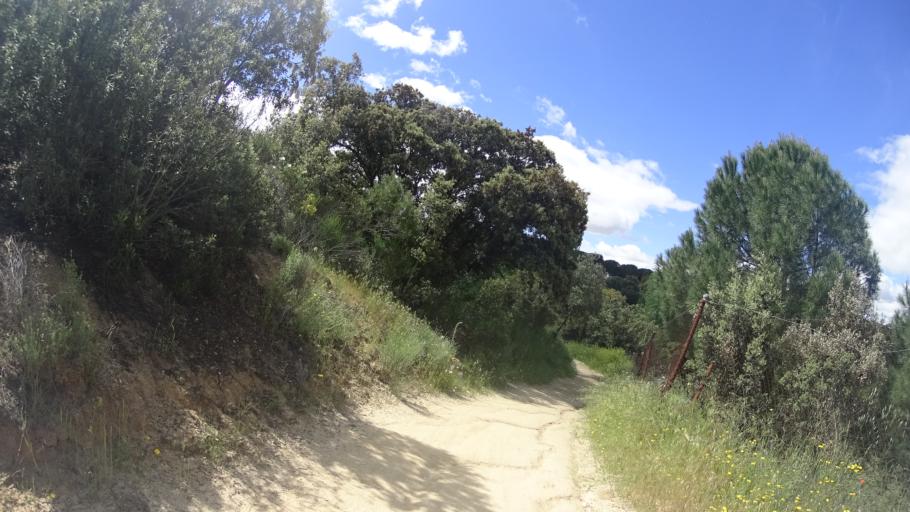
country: ES
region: Madrid
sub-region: Provincia de Madrid
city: Villaviciosa de Odon
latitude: 40.3892
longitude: -3.9400
